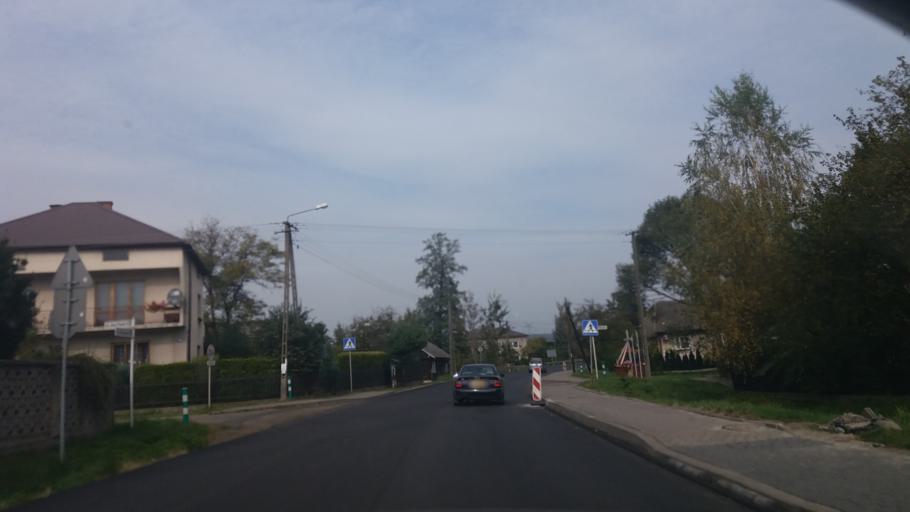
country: PL
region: Lesser Poland Voivodeship
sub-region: Powiat chrzanowski
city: Babice
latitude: 50.0424
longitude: 19.4407
